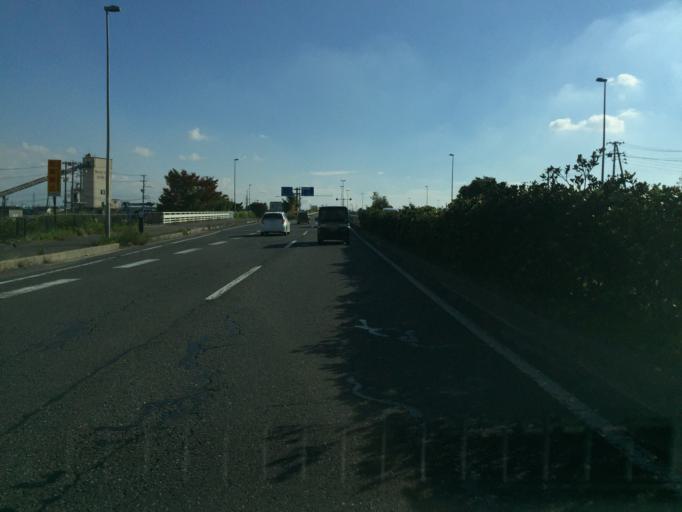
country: JP
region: Fukushima
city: Koriyama
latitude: 37.4476
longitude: 140.3792
